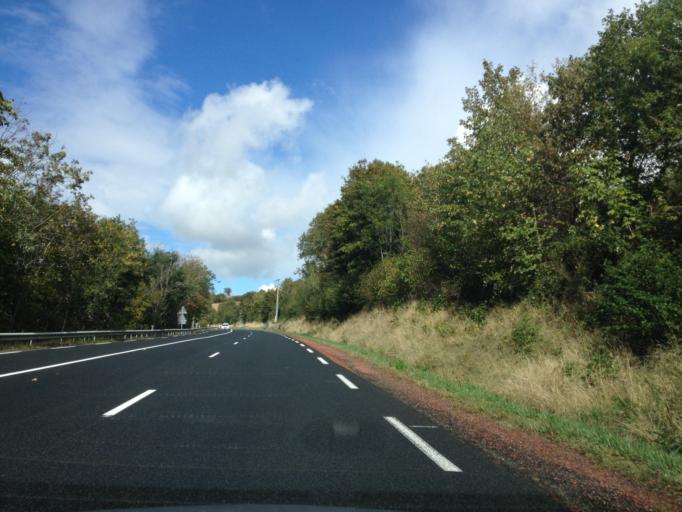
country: FR
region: Rhone-Alpes
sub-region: Departement de la Loire
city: Violay
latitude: 45.9100
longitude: 4.3566
